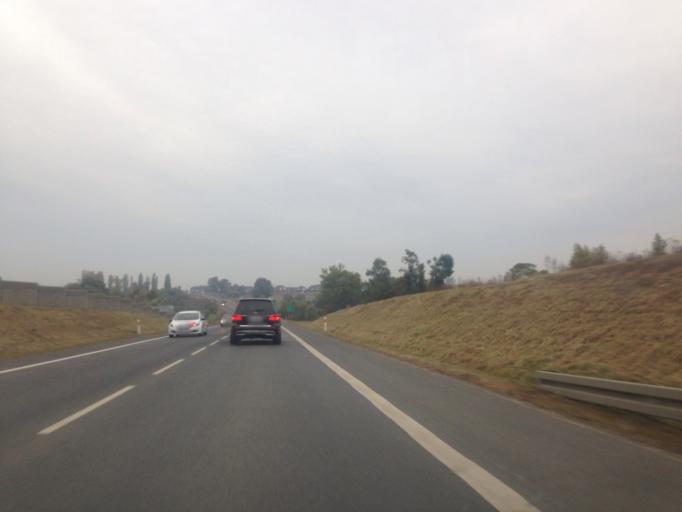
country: PL
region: Greater Poland Voivodeship
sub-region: Powiat gnieznienski
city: Niechanowo
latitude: 52.5544
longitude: 17.6968
